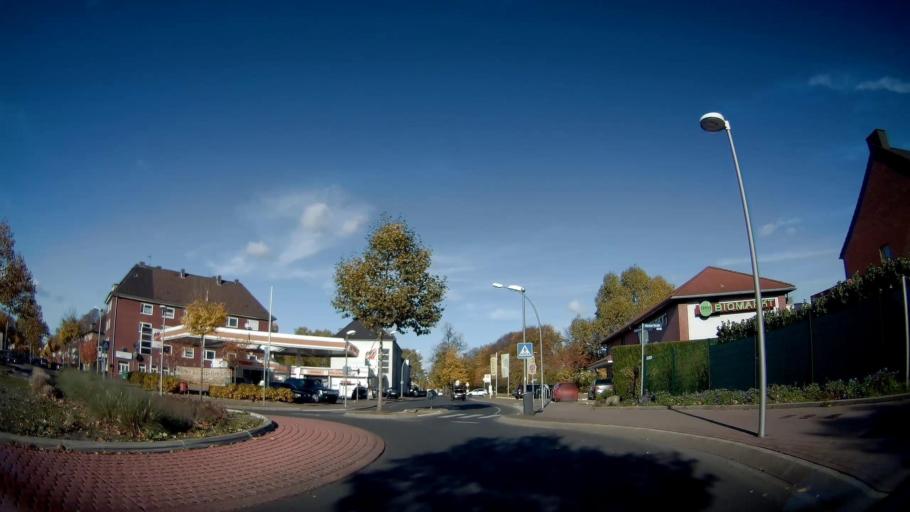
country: DE
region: North Rhine-Westphalia
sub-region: Regierungsbezirk Munster
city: Gladbeck
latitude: 51.5502
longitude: 7.0089
